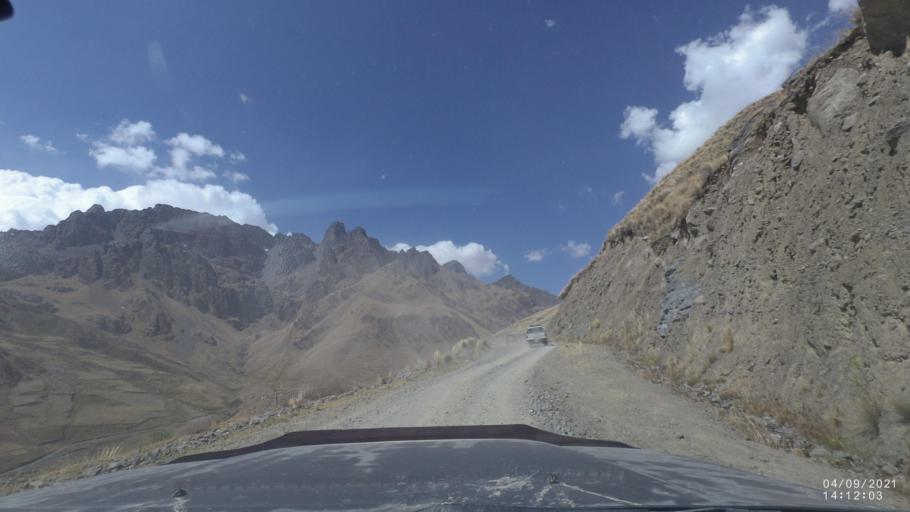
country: BO
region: Cochabamba
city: Sipe Sipe
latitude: -17.2244
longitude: -66.4536
